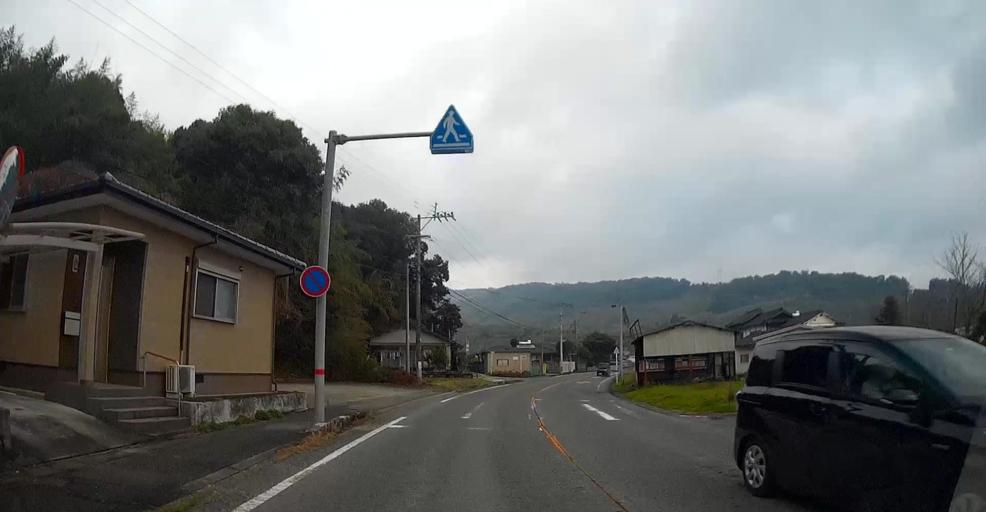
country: JP
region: Kumamoto
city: Matsubase
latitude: 32.6314
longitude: 130.6130
